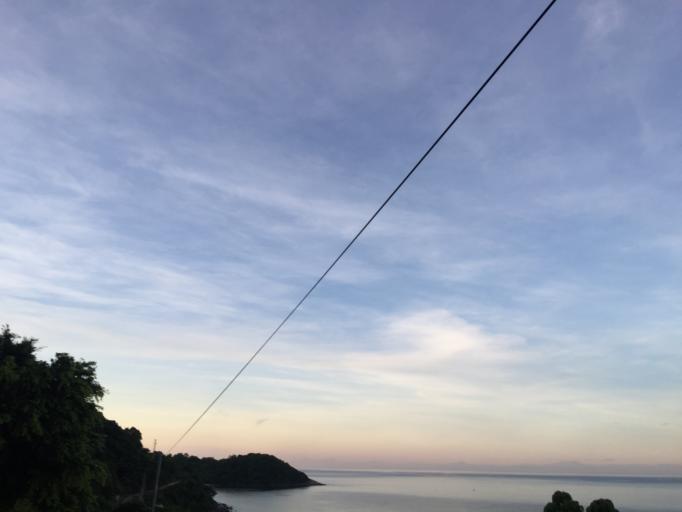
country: VN
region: Quang Nam
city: Hoi An
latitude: 15.9524
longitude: 108.5085
